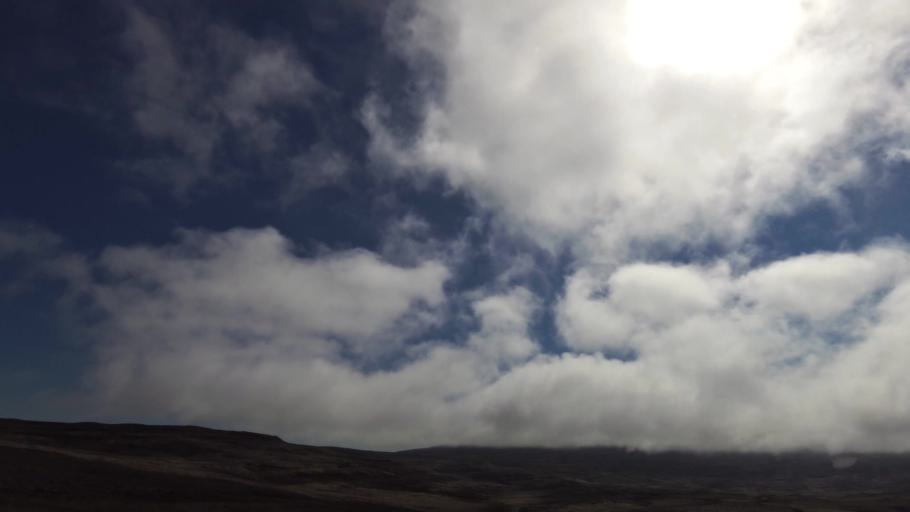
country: IS
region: West
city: Olafsvik
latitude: 65.5550
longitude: -24.2597
